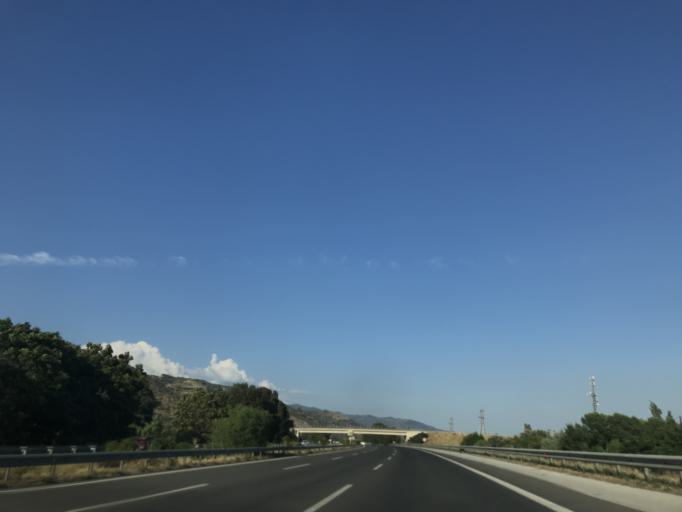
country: TR
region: Aydin
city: Incirliova
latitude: 37.8681
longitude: 27.7256
